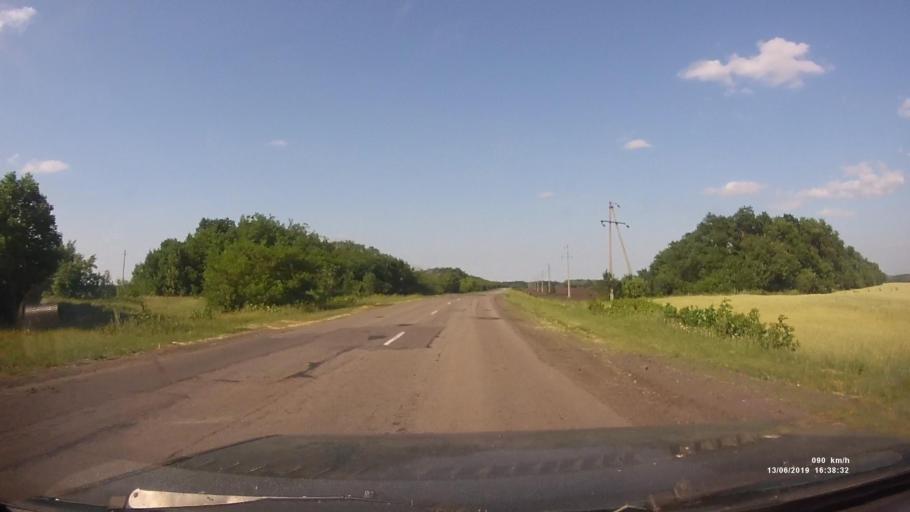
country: RU
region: Rostov
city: Kazanskaya
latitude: 49.9197
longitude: 41.3252
